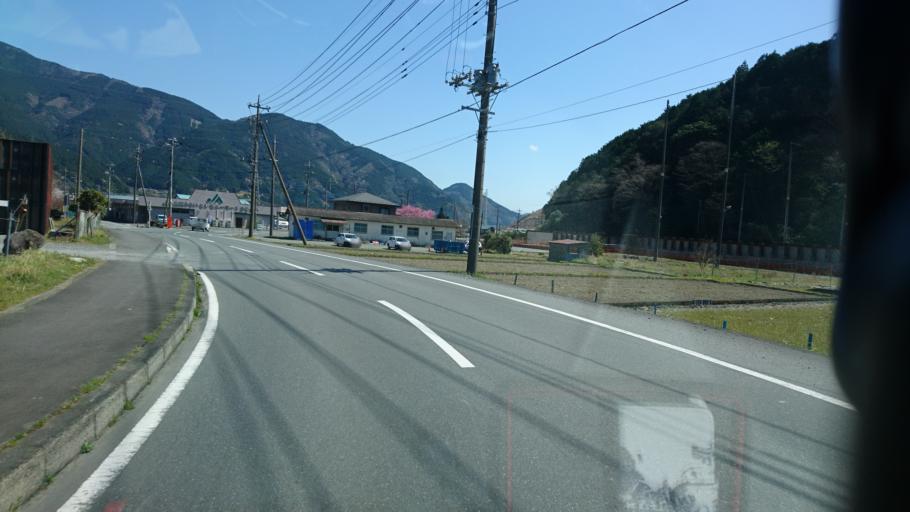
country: JP
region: Shizuoka
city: Fujinomiya
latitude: 35.2843
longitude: 138.4495
